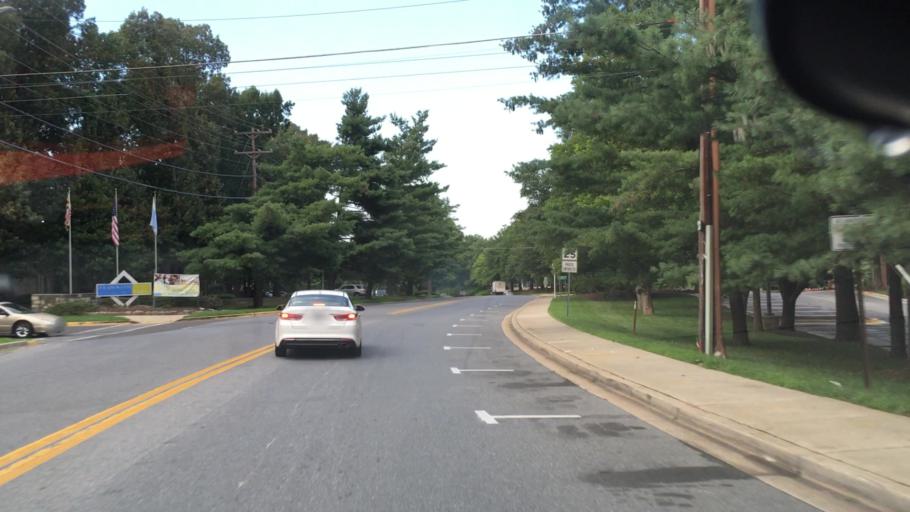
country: US
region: Maryland
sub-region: Prince George's County
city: Berwyn Heights
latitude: 38.9984
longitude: -76.9005
